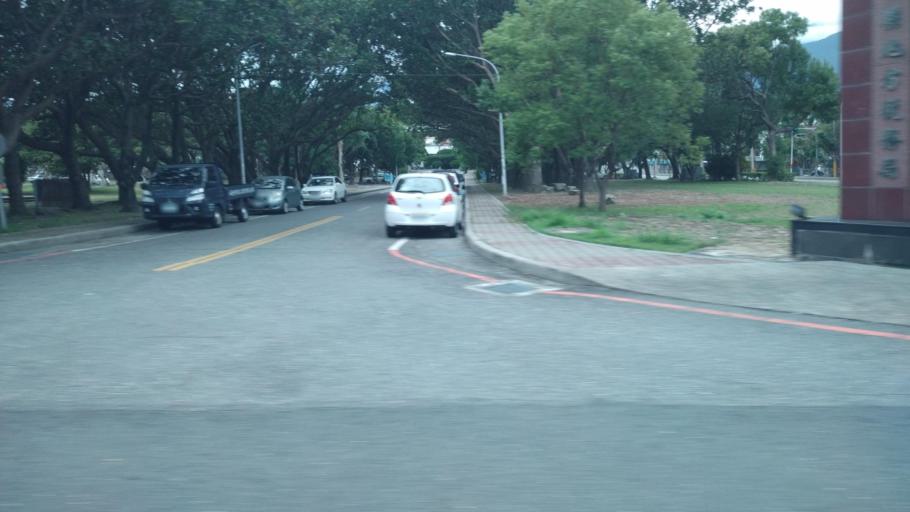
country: TW
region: Taiwan
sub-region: Hualien
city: Hualian
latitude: 23.9923
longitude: 121.6219
